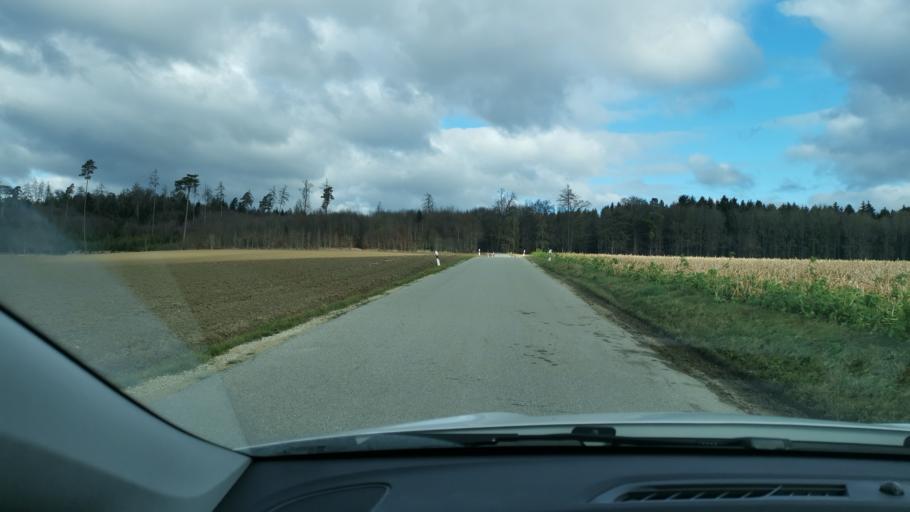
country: DE
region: Bavaria
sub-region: Swabia
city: Aindling
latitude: 48.5370
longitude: 10.9685
